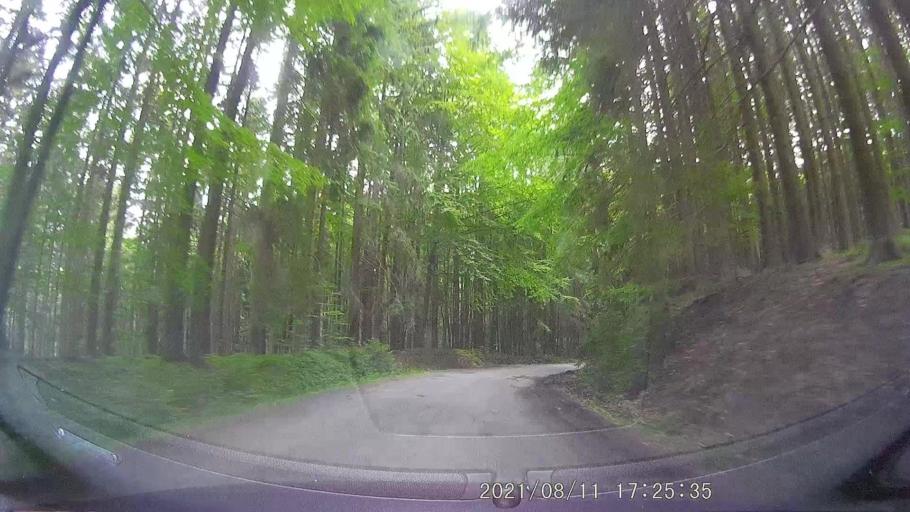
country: PL
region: Lower Silesian Voivodeship
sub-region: Powiat klodzki
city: Polanica-Zdroj
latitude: 50.3063
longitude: 16.4966
